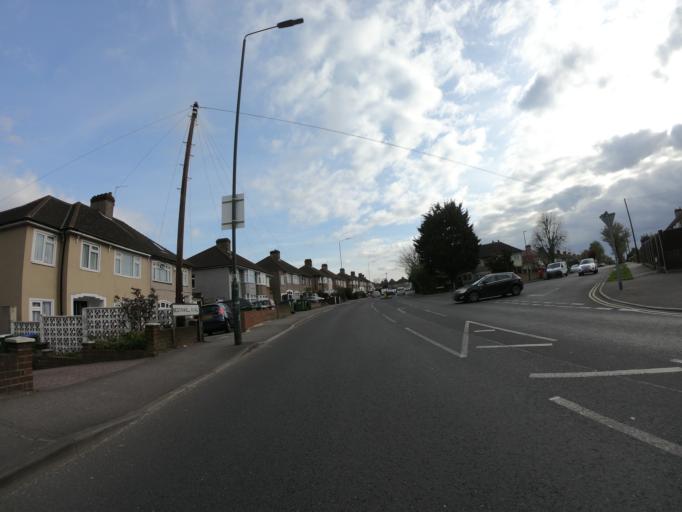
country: GB
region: England
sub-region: Greater London
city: Bexleyheath
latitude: 51.4770
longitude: 0.1453
